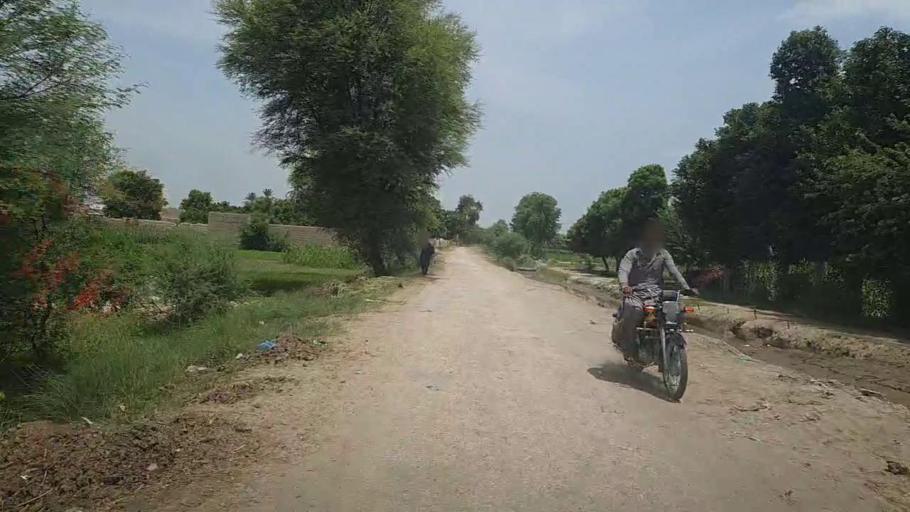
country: PK
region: Sindh
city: Ubauro
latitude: 28.2944
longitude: 69.8009
